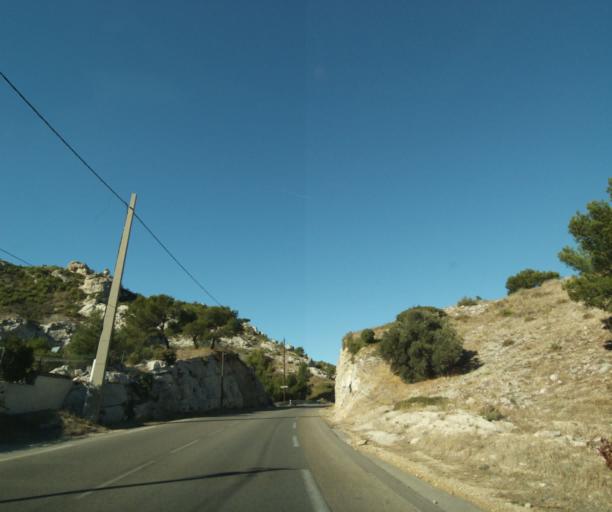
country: FR
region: Provence-Alpes-Cote d'Azur
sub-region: Departement des Bouches-du-Rhone
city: Le Rove
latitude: 43.3596
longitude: 5.2733
